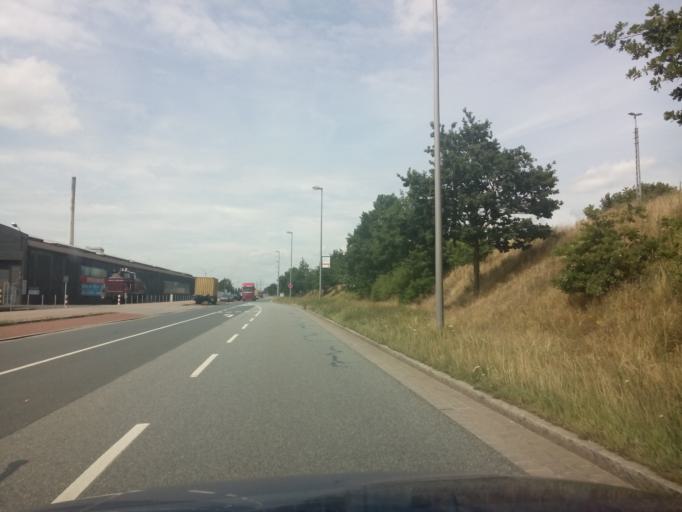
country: DE
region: Lower Saxony
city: Ritterhude
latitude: 53.1216
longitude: 8.7474
